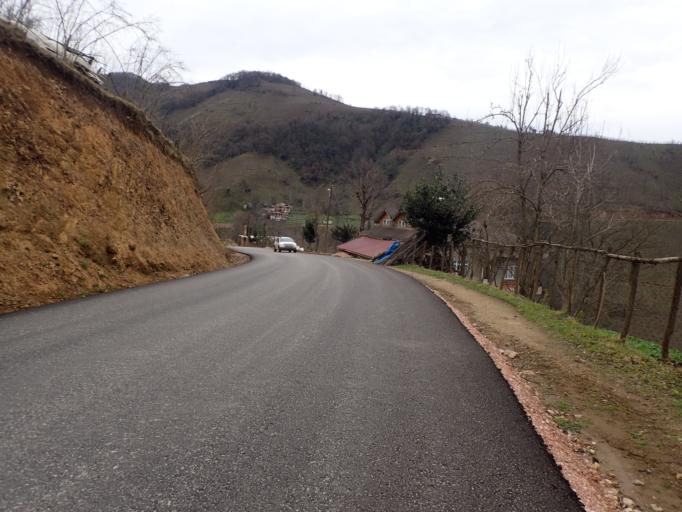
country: TR
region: Ordu
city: Camas
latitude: 40.8859
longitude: 37.5162
